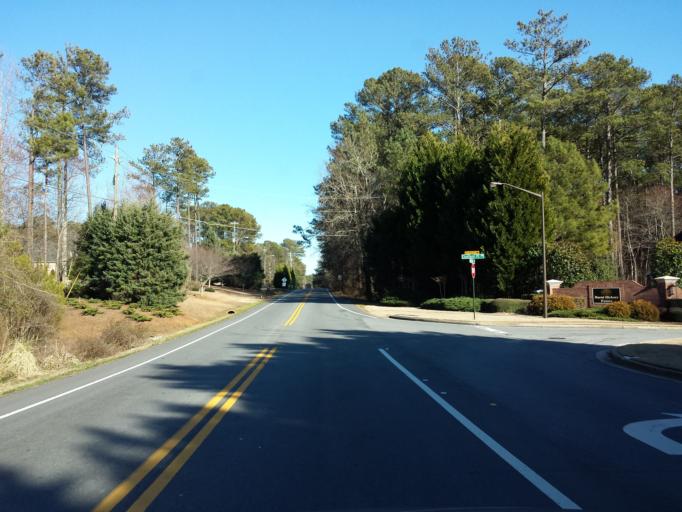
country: US
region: Georgia
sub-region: Cobb County
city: Kennesaw
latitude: 33.9677
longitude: -84.6367
